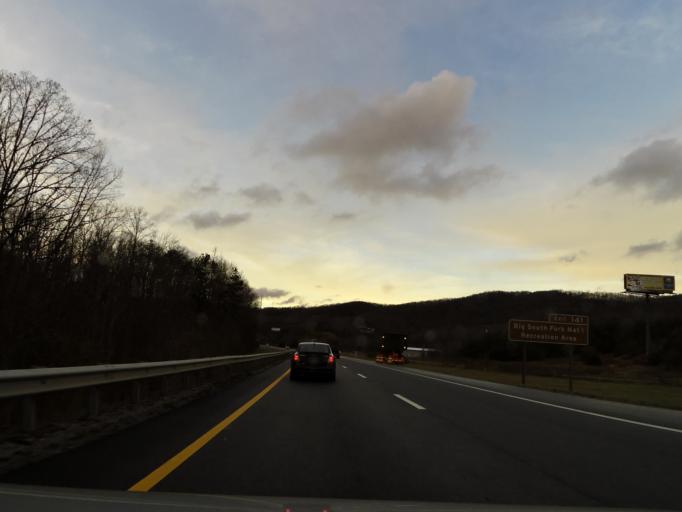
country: US
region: Tennessee
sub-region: Campbell County
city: Jacksboro
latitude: 36.3639
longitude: -84.2316
